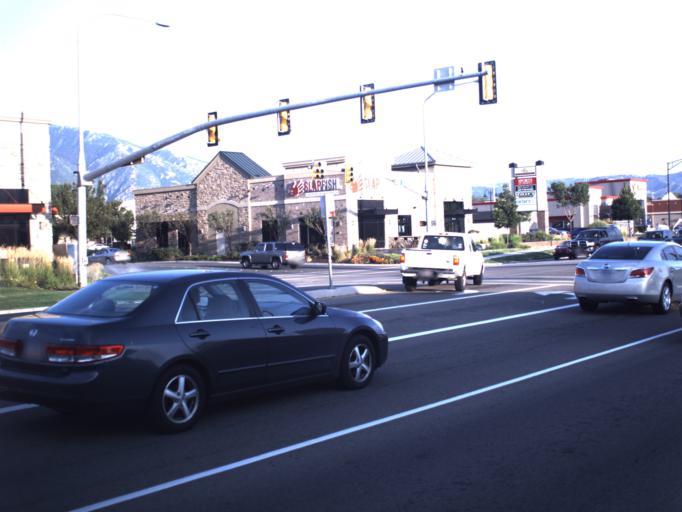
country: US
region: Utah
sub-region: Salt Lake County
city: White City
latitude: 40.5627
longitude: -111.8910
